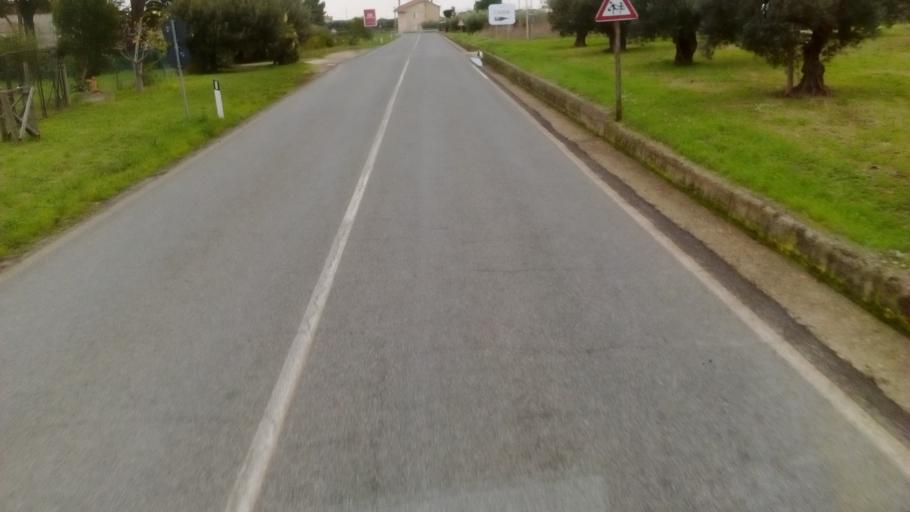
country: IT
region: Abruzzo
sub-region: Provincia di Chieti
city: Vasto
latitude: 42.1653
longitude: 14.6664
